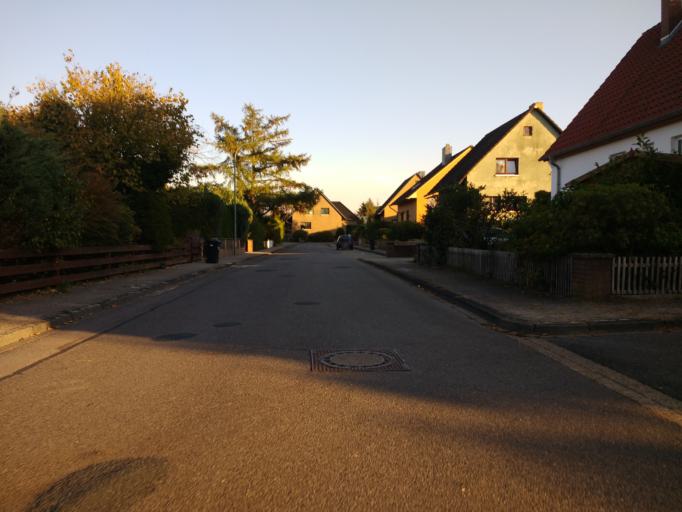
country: DE
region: Lower Saxony
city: Gifhorn
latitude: 52.4862
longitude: 10.5594
